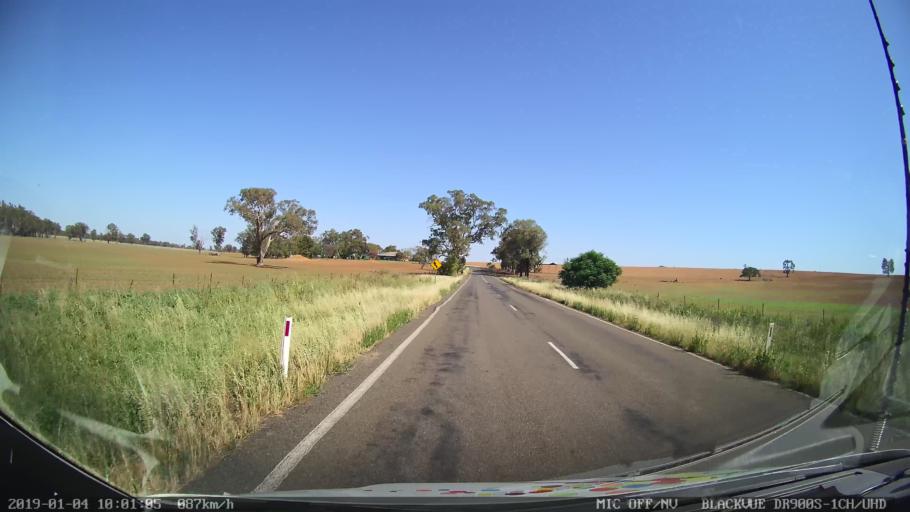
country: AU
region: New South Wales
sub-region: Cabonne
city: Canowindra
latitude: -33.4904
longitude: 148.3742
